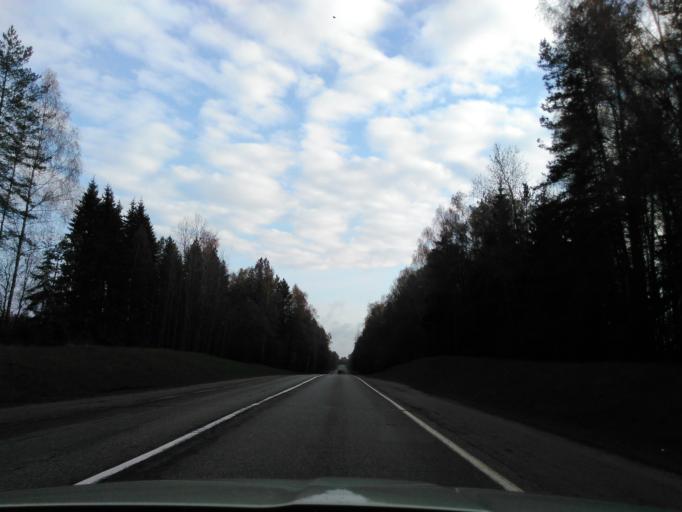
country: BY
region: Minsk
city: Lahoysk
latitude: 54.3054
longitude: 27.8752
